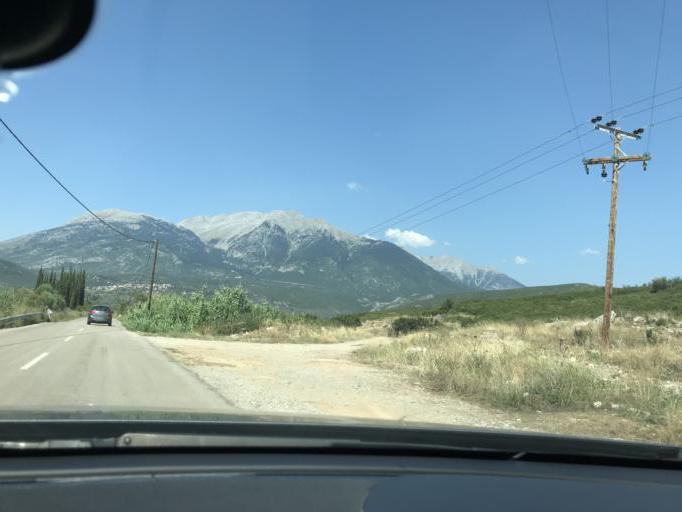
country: GR
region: Central Greece
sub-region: Nomos Fthiotidos
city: Kato Tithorea
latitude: 38.5215
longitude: 22.7750
